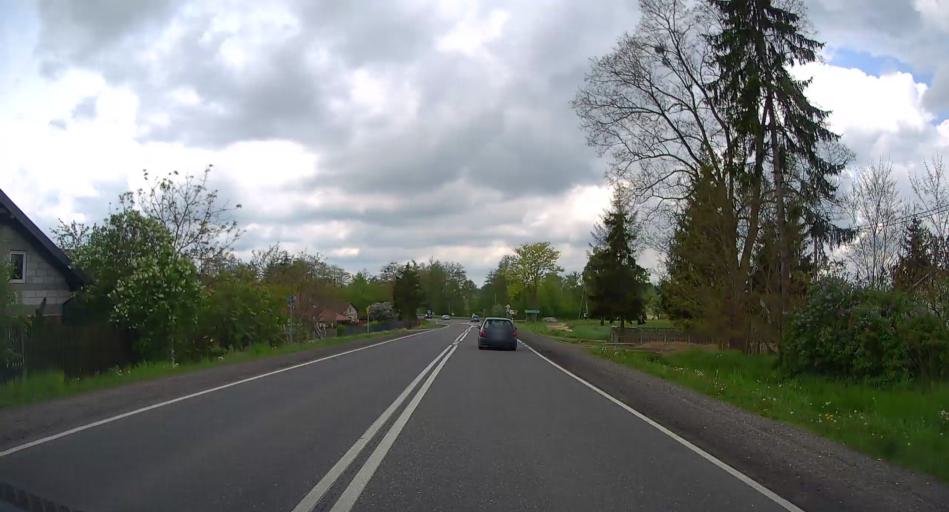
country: PL
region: Masovian Voivodeship
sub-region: Powiat plonski
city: Zaluski
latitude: 52.4315
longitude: 20.4562
